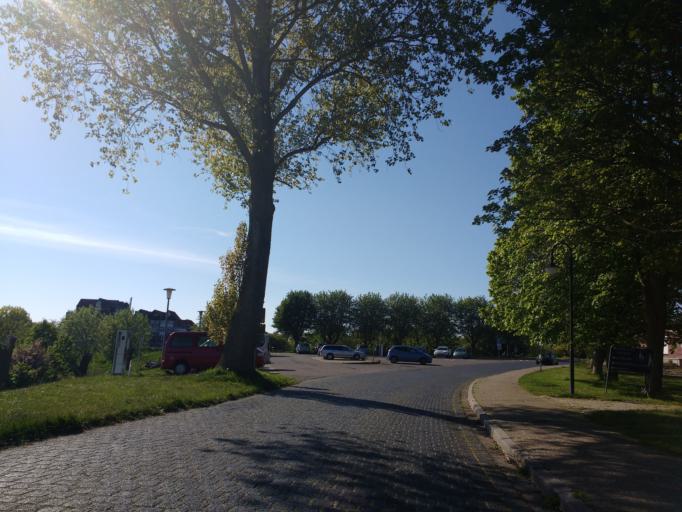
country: DE
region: Lower Saxony
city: Schillig
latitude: 53.6845
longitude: 8.0180
